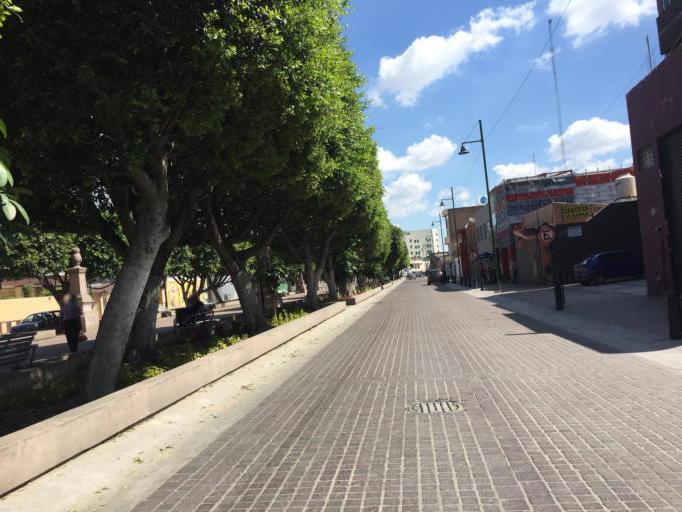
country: MX
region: Guanajuato
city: Leon
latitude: 21.1181
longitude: -101.6699
